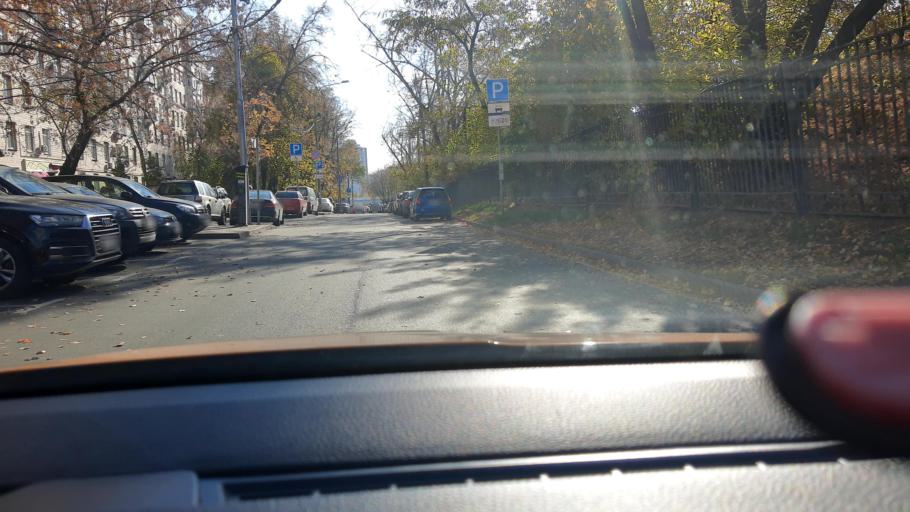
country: RU
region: Moscow
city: Vorob'yovo
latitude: 55.7348
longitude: 37.5175
